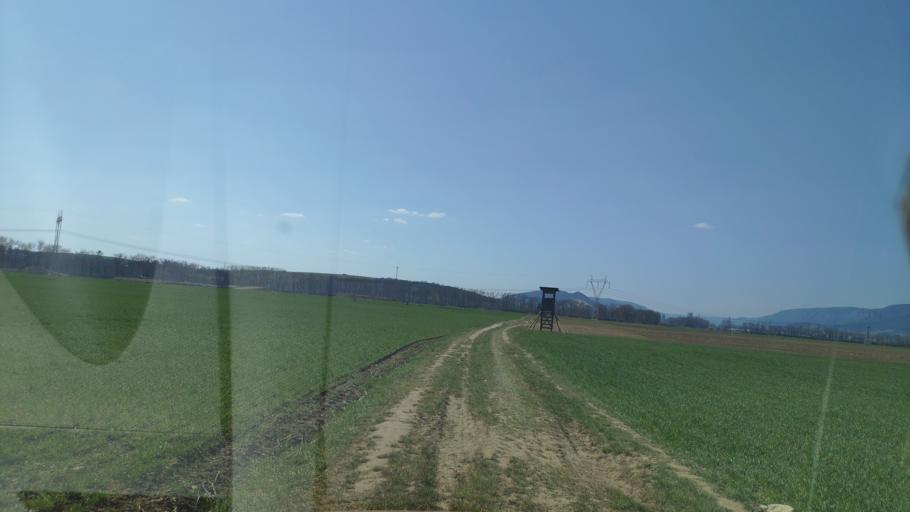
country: SK
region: Kosicky
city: Moldava nad Bodvou
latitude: 48.5959
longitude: 20.9377
